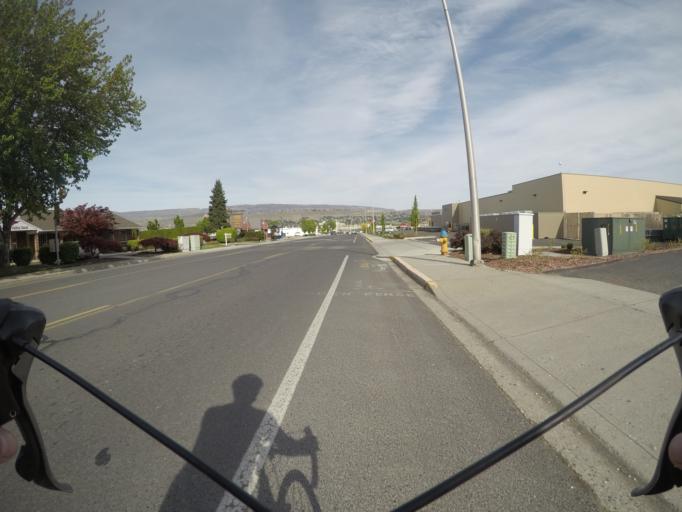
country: US
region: Washington
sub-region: Chelan County
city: West Wenatchee
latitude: 47.4423
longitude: -120.3290
